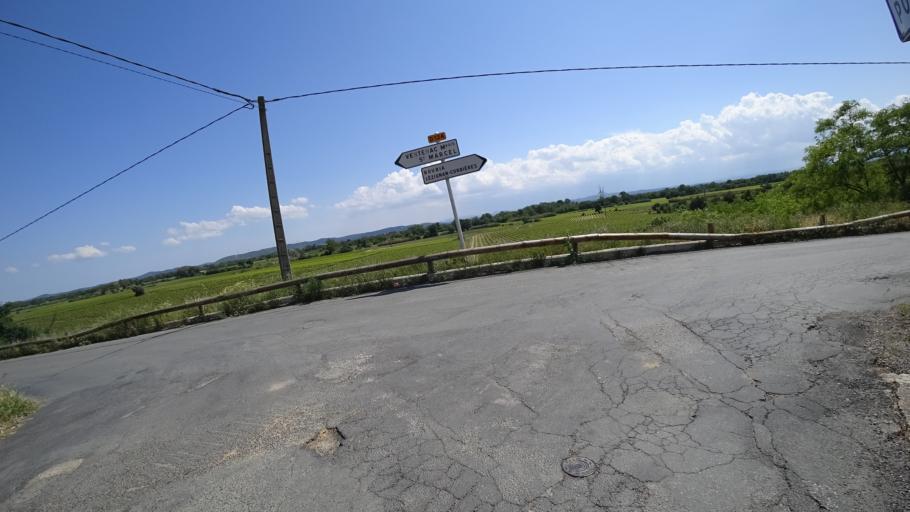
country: FR
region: Languedoc-Roussillon
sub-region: Departement de l'Aude
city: Canet
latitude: 43.2487
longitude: 2.8337
